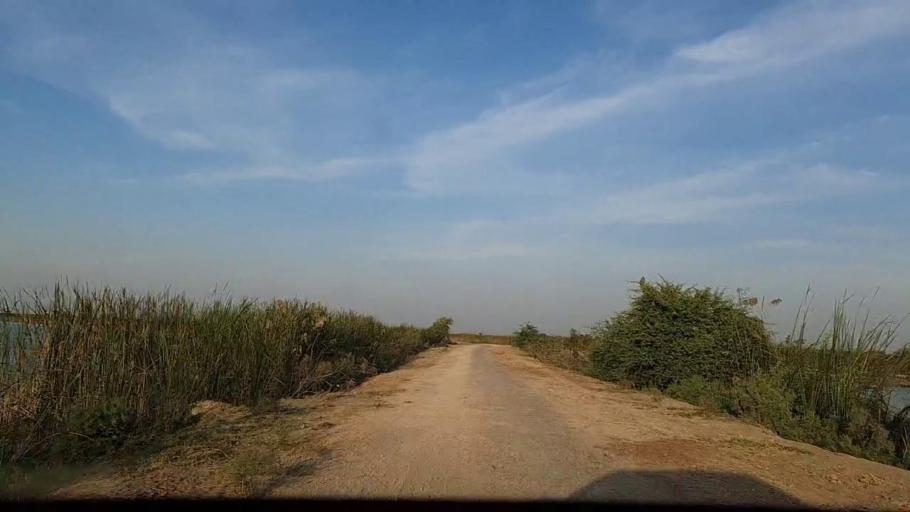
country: PK
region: Sindh
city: Mirpur Batoro
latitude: 24.6540
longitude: 68.1458
